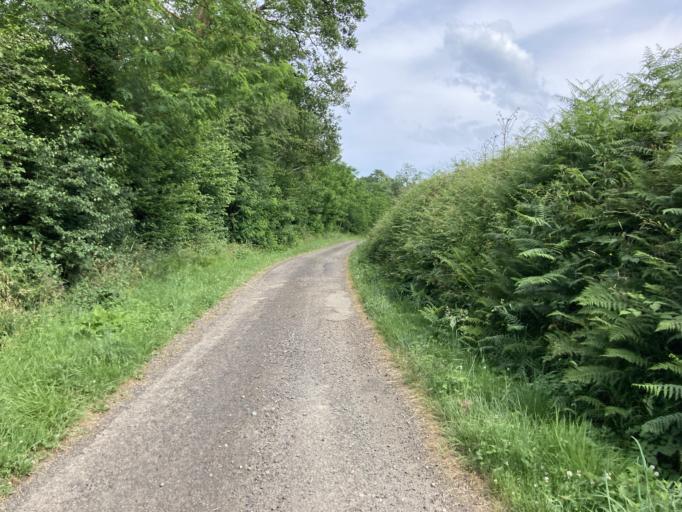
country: FR
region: Aquitaine
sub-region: Departement des Pyrenees-Atlantiques
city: Lucq-de-Bearn
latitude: 43.2786
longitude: -0.6147
